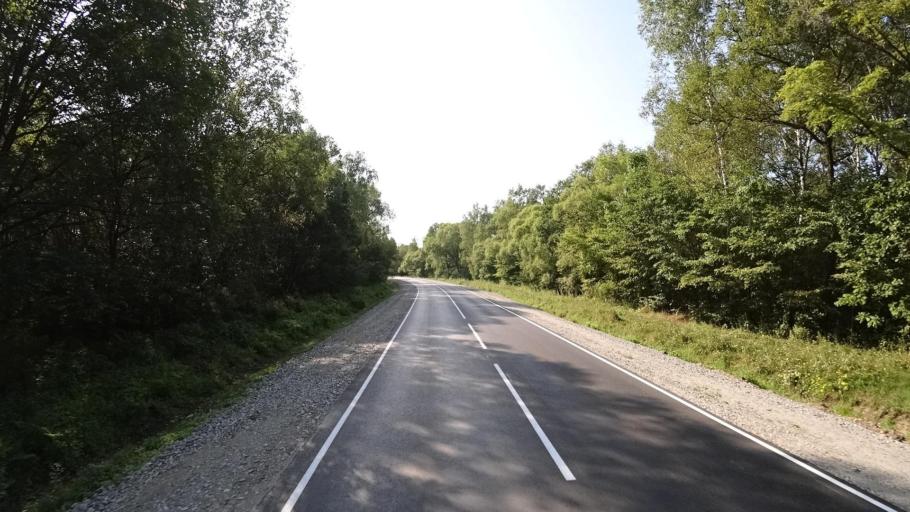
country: RU
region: Khabarovsk Krai
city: Khor
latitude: 47.9766
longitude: 135.0757
